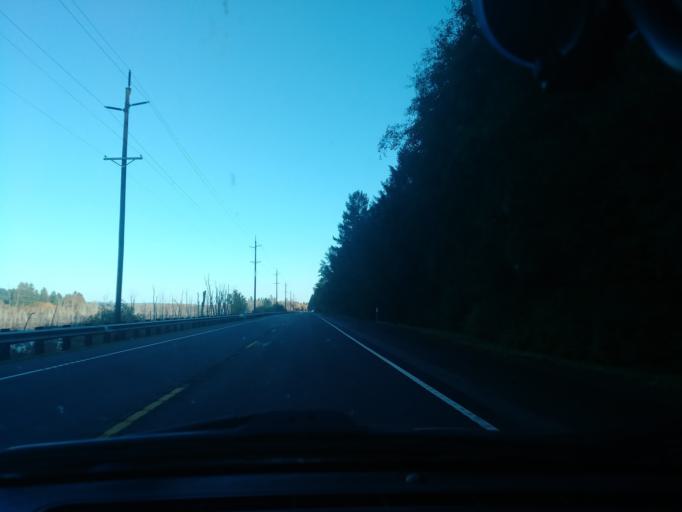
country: US
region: Oregon
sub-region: Washington County
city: Banks
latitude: 45.6111
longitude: -123.1549
